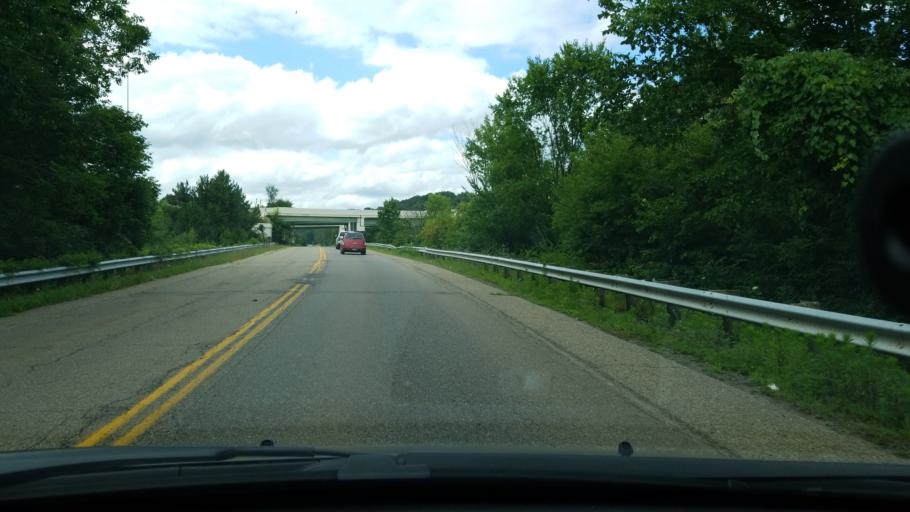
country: US
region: Ohio
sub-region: Stark County
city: Canton
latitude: 40.8275
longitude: -81.3956
